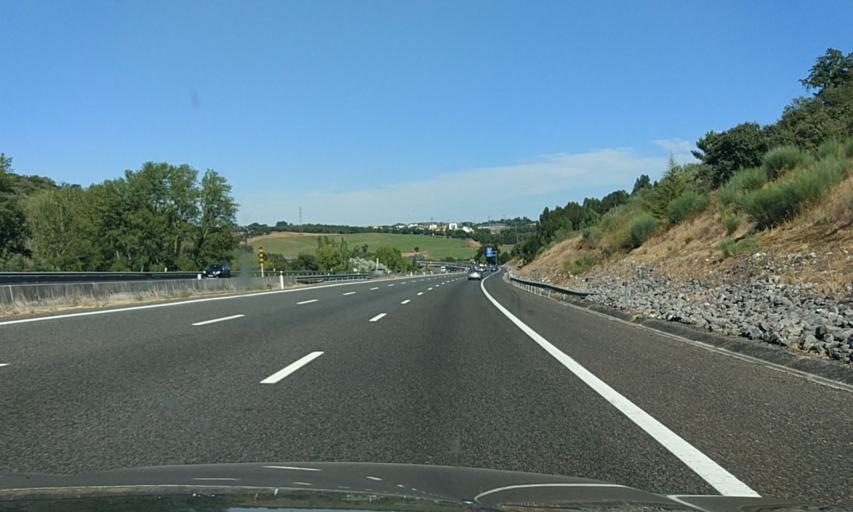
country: PT
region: Santarem
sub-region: Santarem
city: Santarem
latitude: 39.2371
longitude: -8.7544
